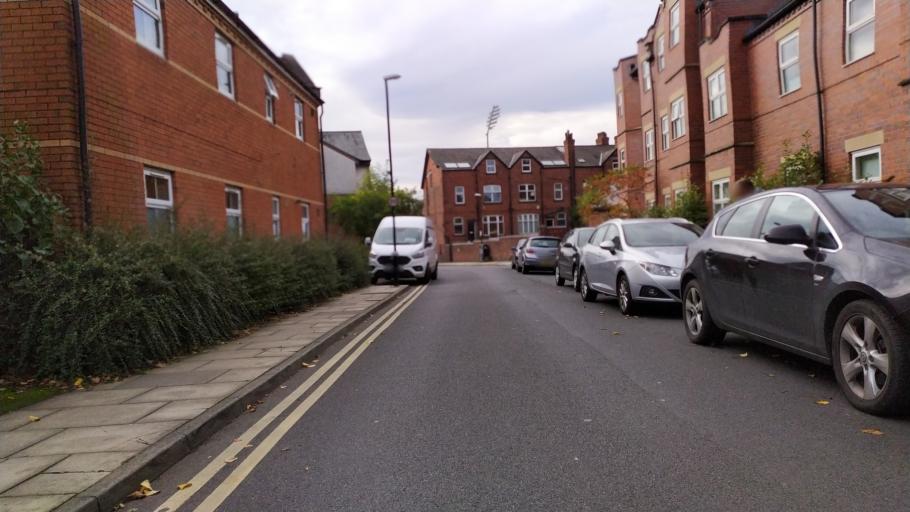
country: GB
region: England
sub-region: City and Borough of Leeds
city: Leeds
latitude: 53.8185
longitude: -1.5775
